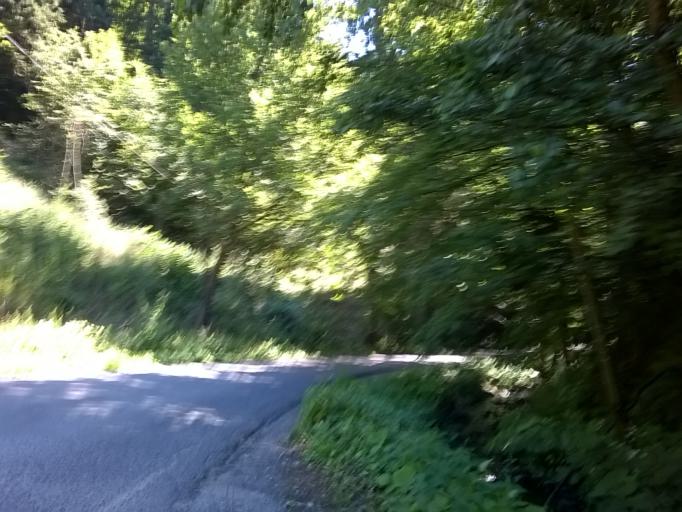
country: SK
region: Banskobystricky
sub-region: Okres Banska Bystrica
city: Banska Stiavnica
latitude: 48.4675
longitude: 18.8429
